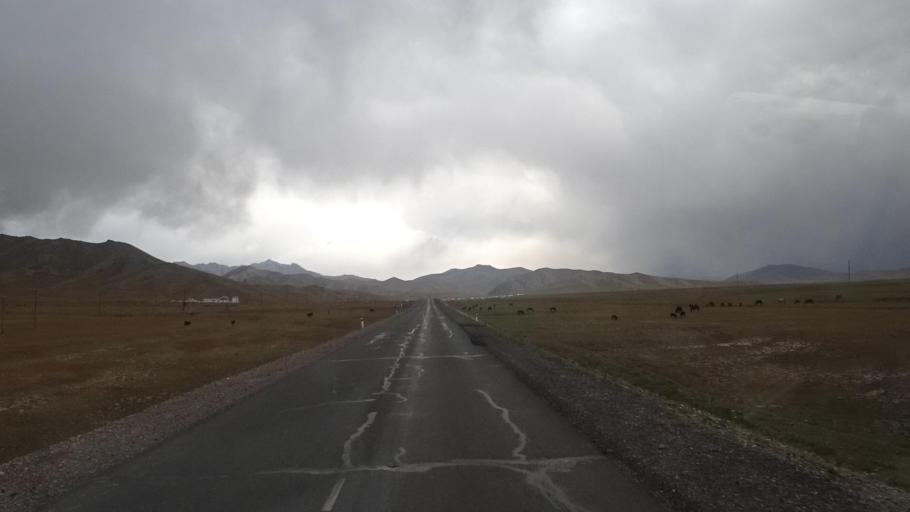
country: KG
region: Osh
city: Gul'cha
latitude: 39.7072
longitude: 73.2308
